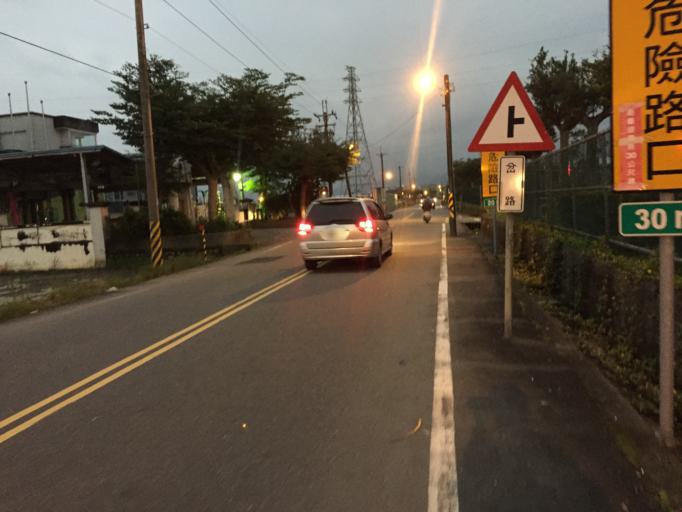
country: TW
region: Taiwan
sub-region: Yilan
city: Yilan
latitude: 24.6604
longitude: 121.7785
